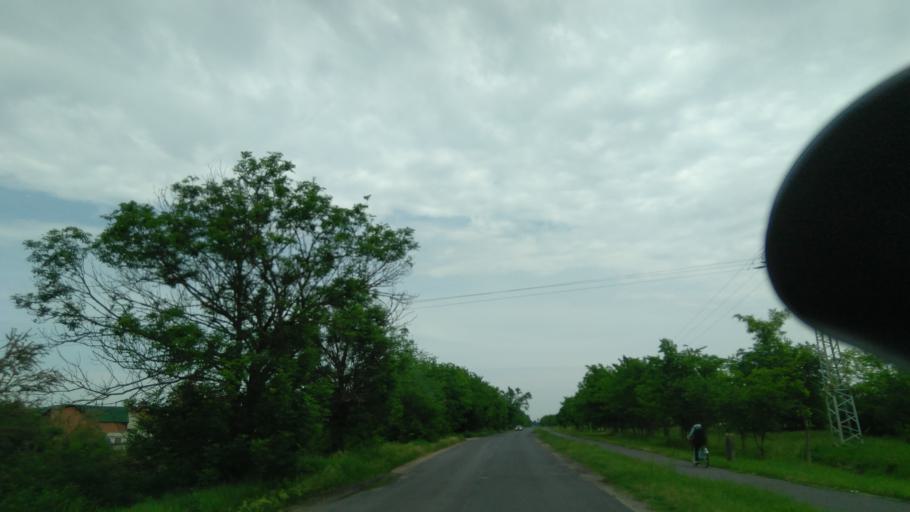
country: HU
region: Bekes
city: Szeghalom
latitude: 47.0378
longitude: 21.1832
